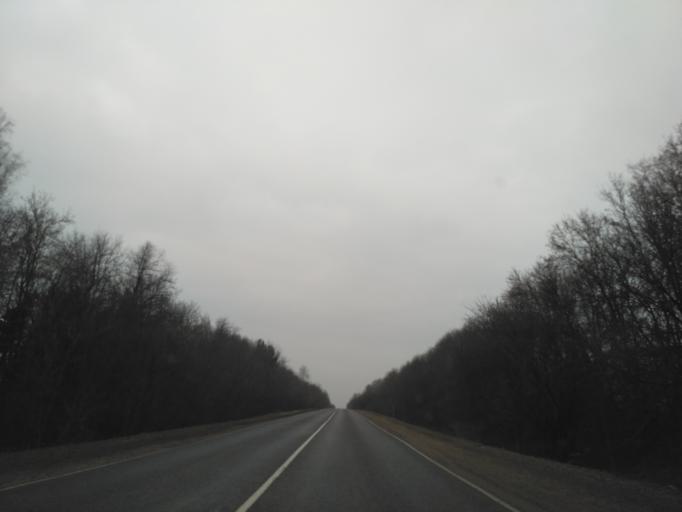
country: BY
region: Minsk
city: Haradzyeya
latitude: 53.3220
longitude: 26.4397
